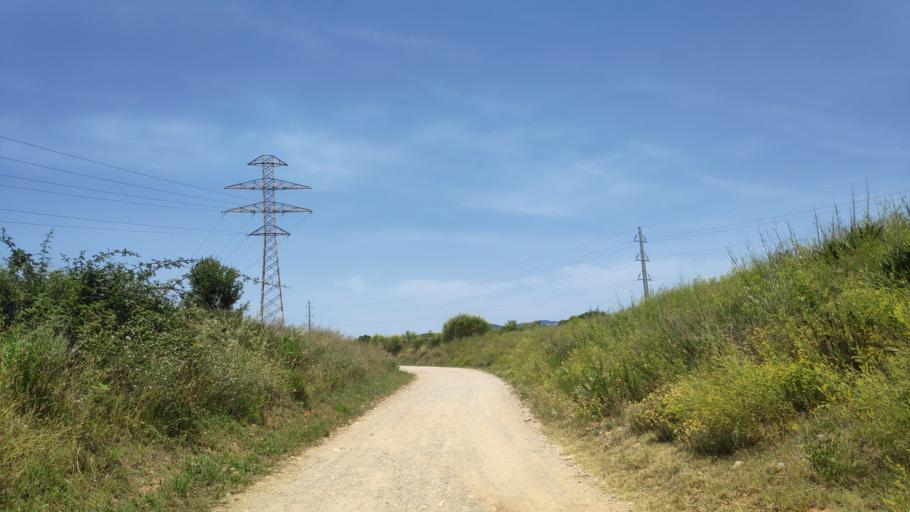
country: ES
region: Catalonia
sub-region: Provincia de Barcelona
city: Sant Quirze del Valles
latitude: 41.5647
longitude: 2.0620
